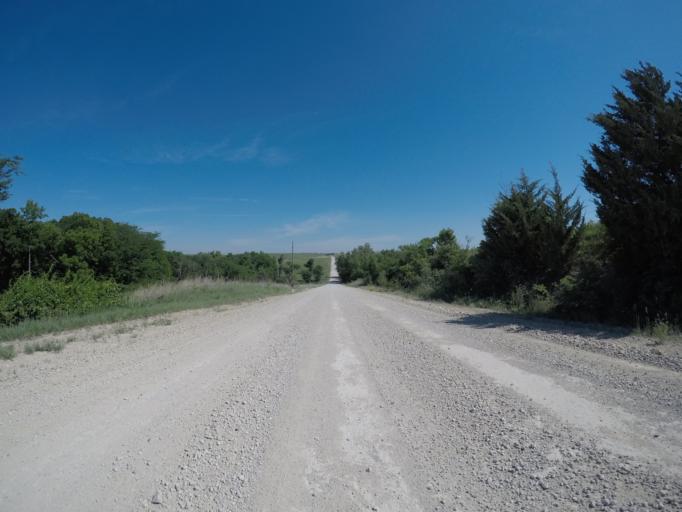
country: US
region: Kansas
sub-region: Wabaunsee County
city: Alma
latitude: 39.0054
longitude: -96.1137
